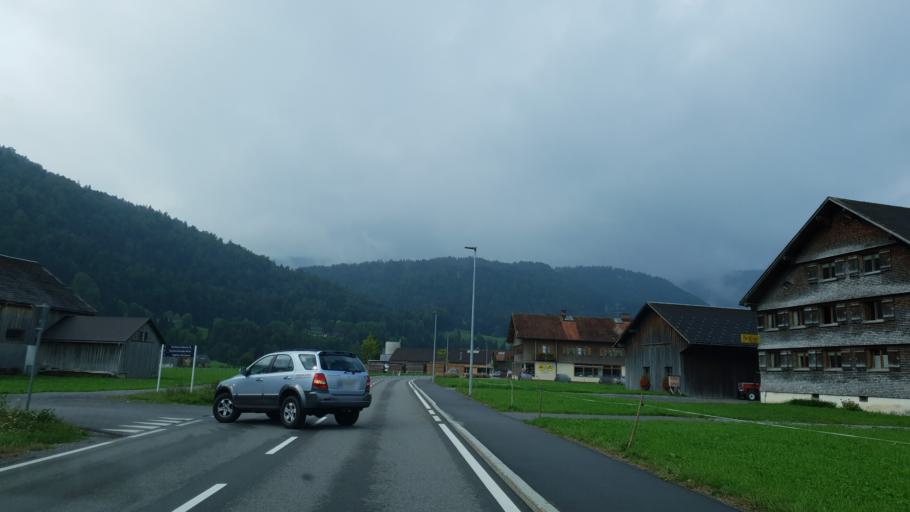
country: AT
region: Vorarlberg
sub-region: Politischer Bezirk Bregenz
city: Andelsbuch
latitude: 47.4083
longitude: 9.8892
